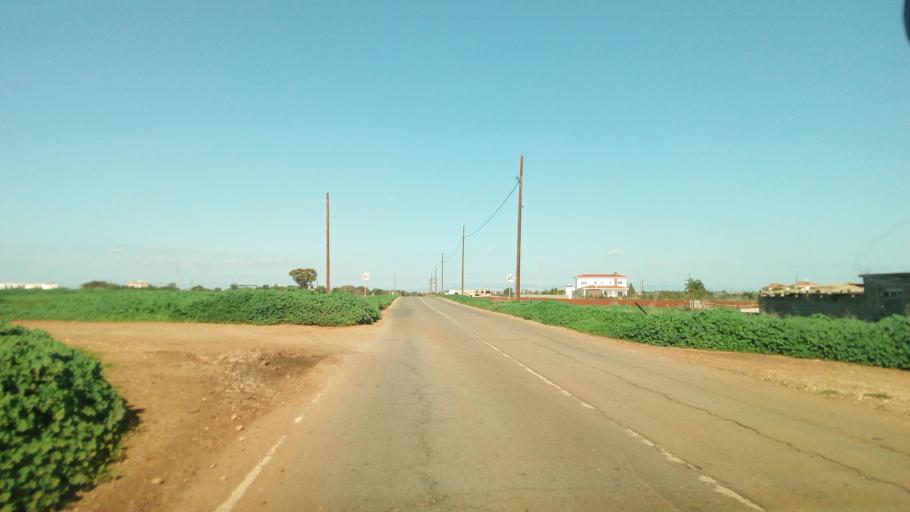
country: CY
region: Ammochostos
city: Avgorou
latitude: 34.9913
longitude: 33.8468
